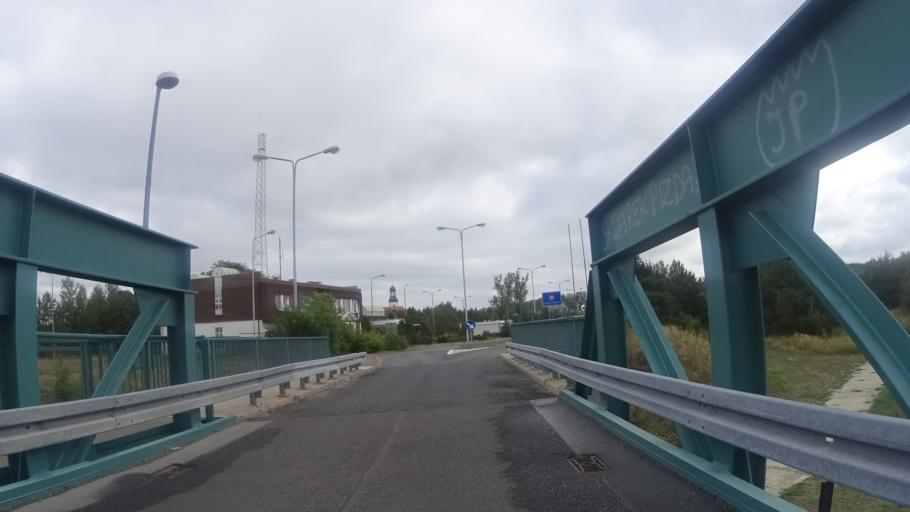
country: PL
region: Lubusz
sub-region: Powiat zarski
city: Przewoz
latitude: 51.4721
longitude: 14.9469
